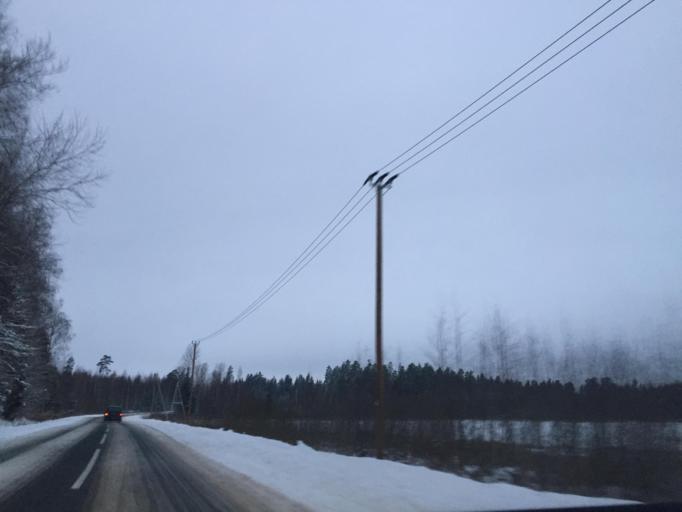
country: LV
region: Raunas
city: Rauna
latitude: 57.4373
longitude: 25.7338
